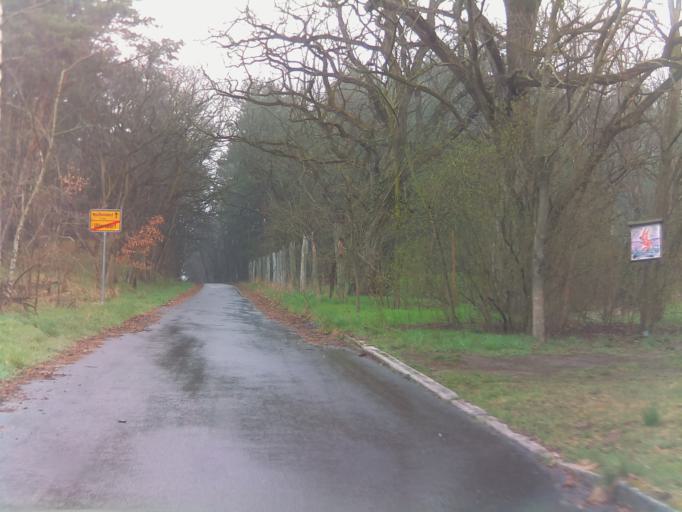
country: DE
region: Brandenburg
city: Jamlitz
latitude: 52.0403
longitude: 14.3667
